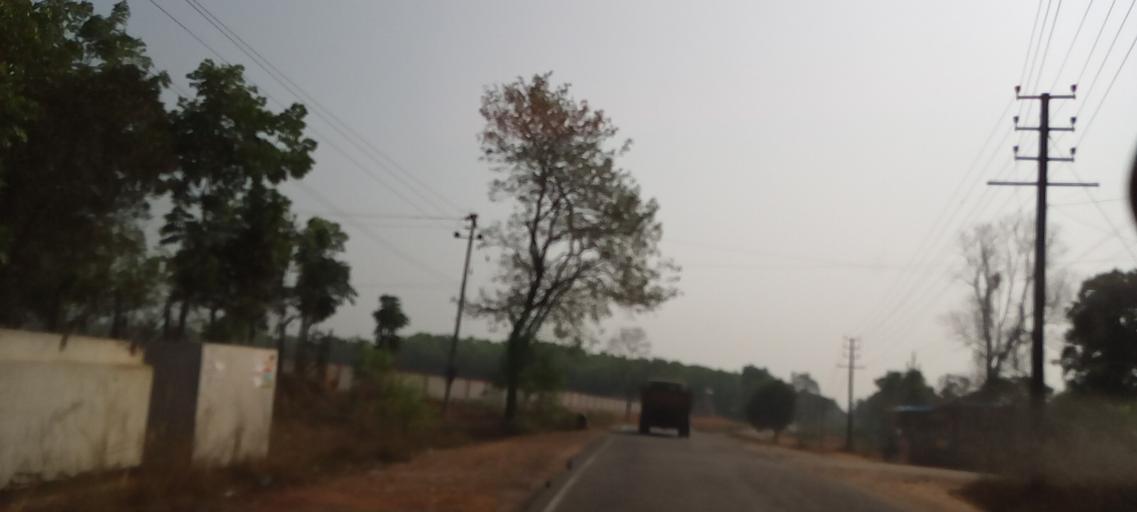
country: IN
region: Karnataka
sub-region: Udupi
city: Coondapoor
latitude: 13.5171
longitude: 74.7597
